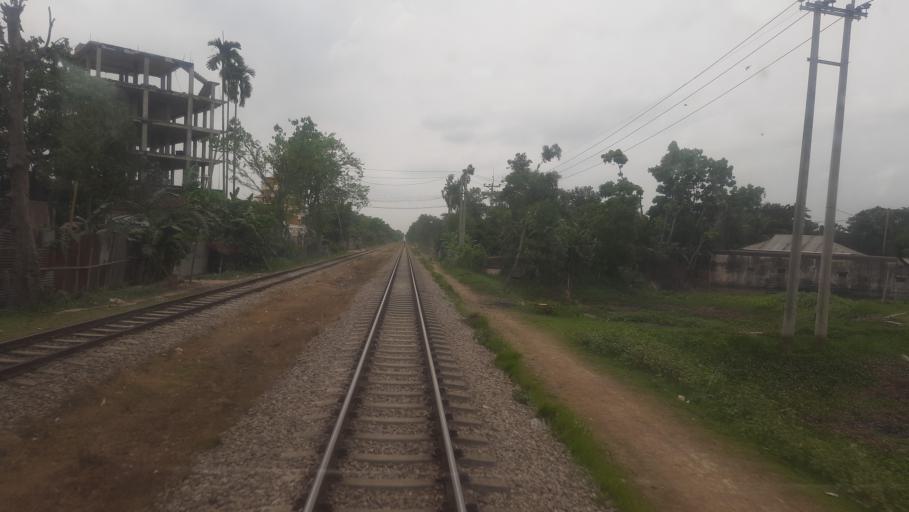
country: BD
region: Chittagong
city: Feni
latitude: 23.0223
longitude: 91.3909
